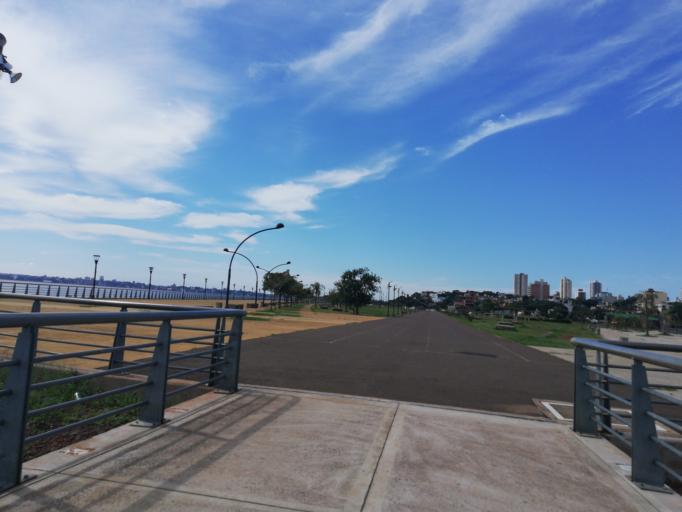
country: AR
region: Misiones
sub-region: Departamento de Capital
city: Posadas
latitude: -27.3520
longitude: -55.9057
